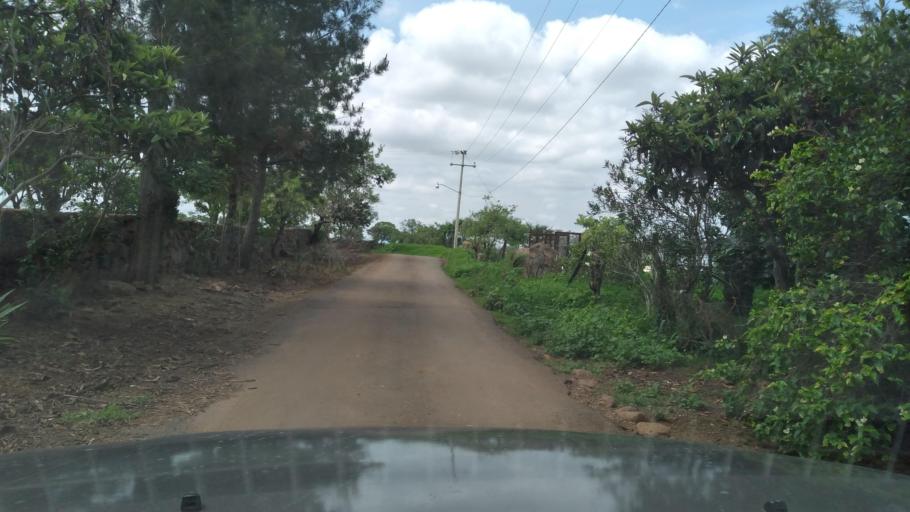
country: MX
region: Jalisco
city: Capilla de Guadalupe
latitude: 20.7487
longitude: -102.6288
